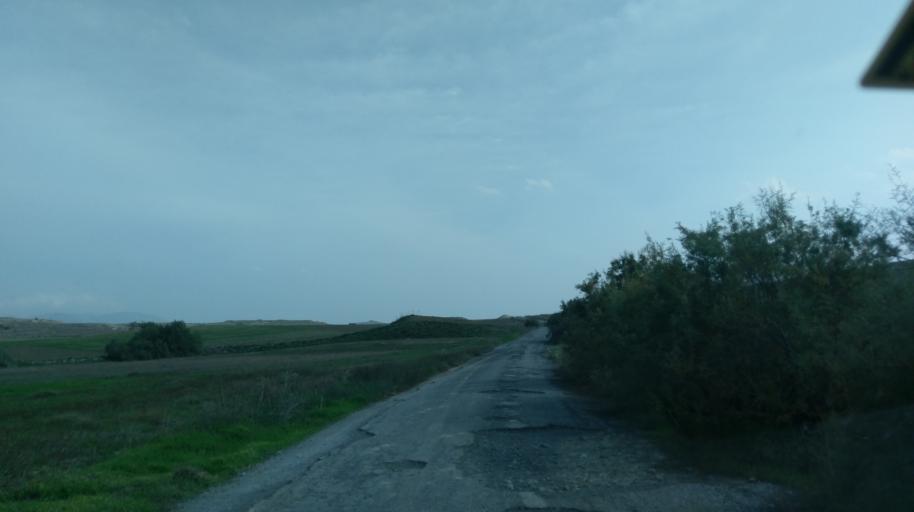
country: CY
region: Keryneia
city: Lapithos
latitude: 35.2630
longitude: 33.0945
